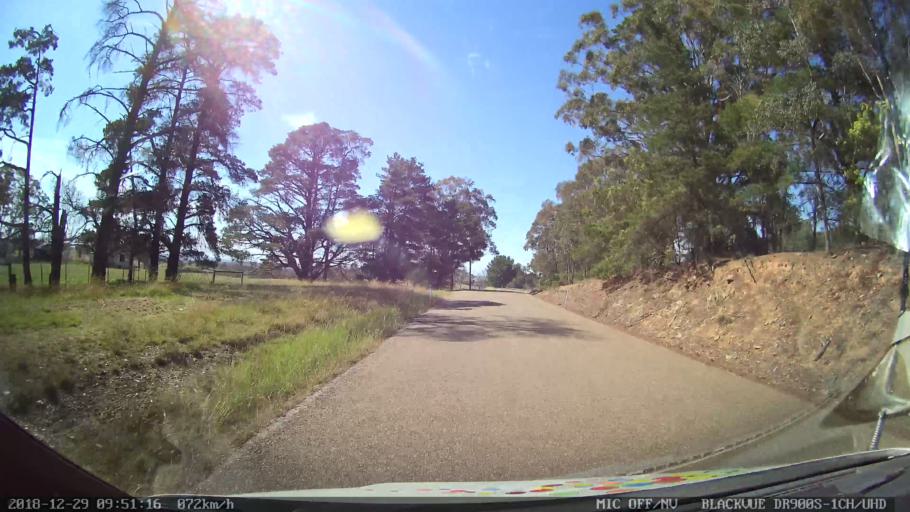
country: AU
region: New South Wales
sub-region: Goulburn Mulwaree
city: Goulburn
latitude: -34.7305
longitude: 149.4617
